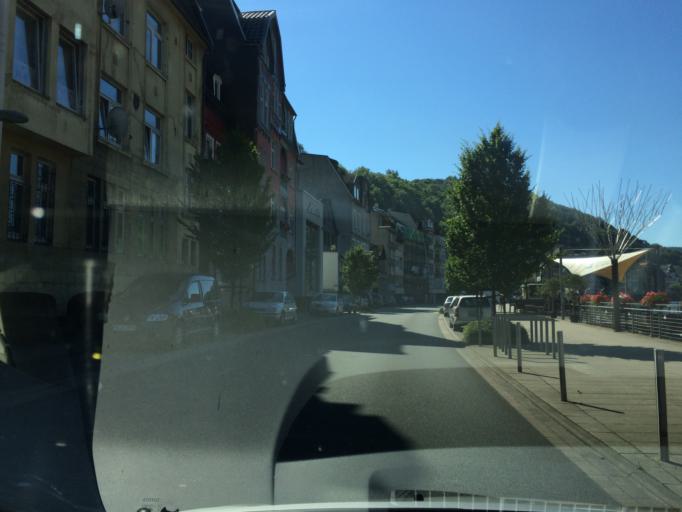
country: DE
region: North Rhine-Westphalia
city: Altena
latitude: 51.3009
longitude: 7.6722
